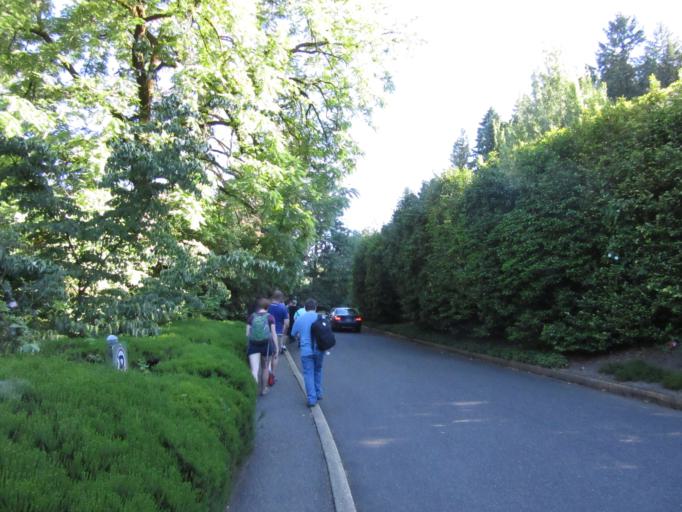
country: US
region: Oregon
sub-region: Multnomah County
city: Portland
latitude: 45.5210
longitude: -122.7051
